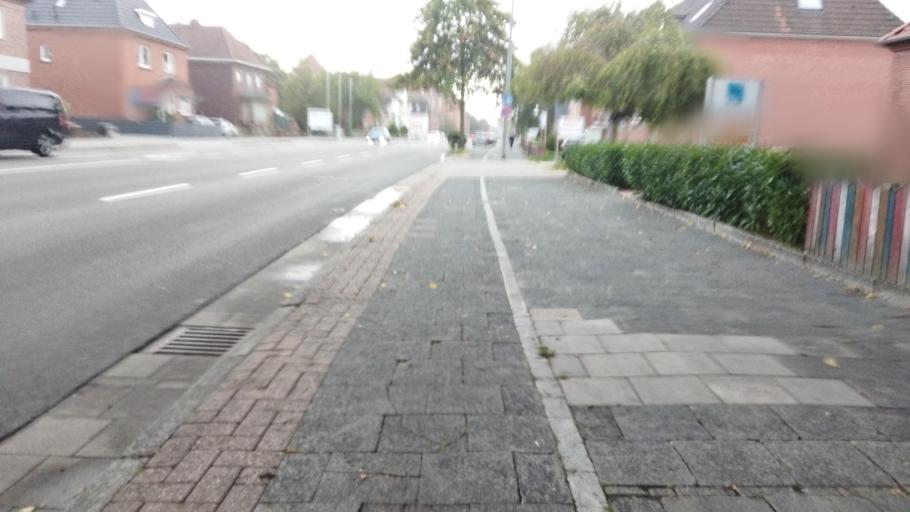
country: DE
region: Lower Saxony
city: Emden
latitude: 53.3848
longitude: 7.2076
